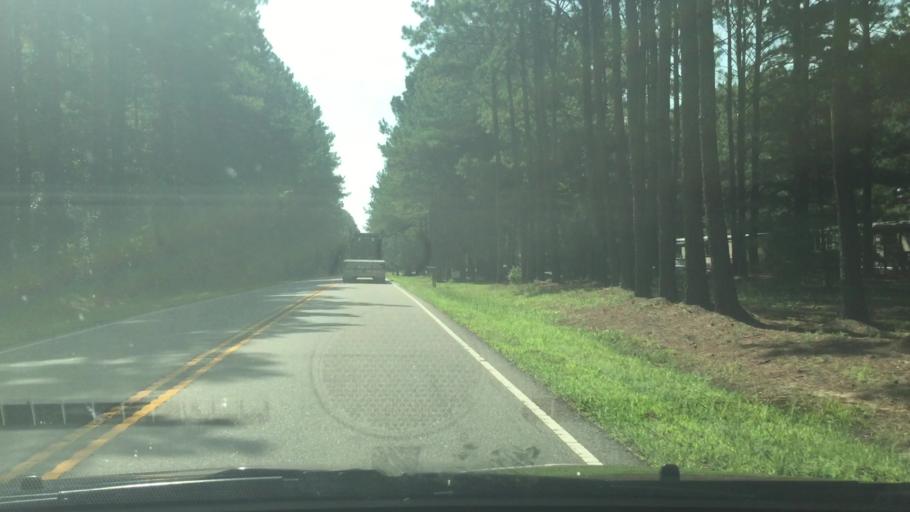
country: US
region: Virginia
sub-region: Sussex County
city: Sussex
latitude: 37.0298
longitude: -77.2977
